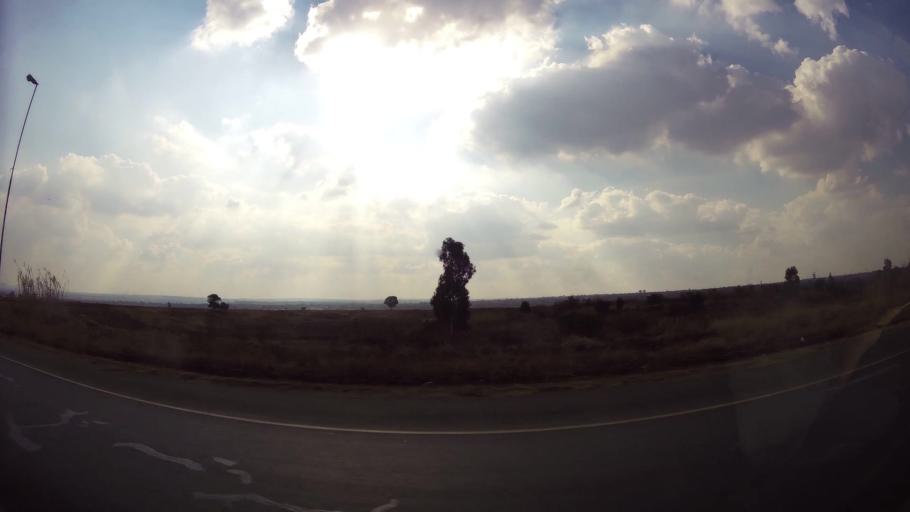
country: ZA
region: Gauteng
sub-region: Ekurhuleni Metropolitan Municipality
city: Boksburg
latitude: -26.2819
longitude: 28.2549
